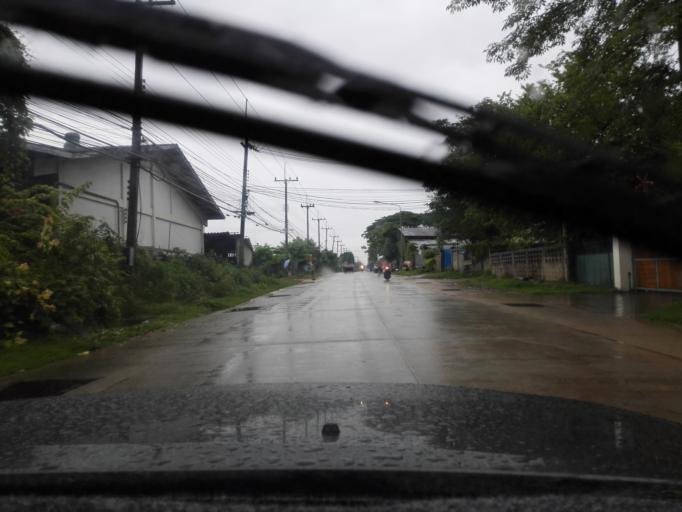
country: TH
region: Tak
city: Mae Sot
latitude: 16.7034
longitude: 98.5722
